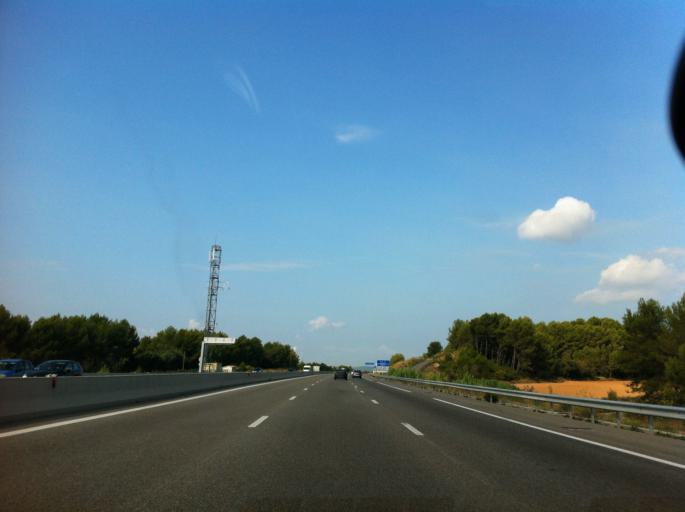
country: FR
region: Provence-Alpes-Cote d'Azur
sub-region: Departement des Bouches-du-Rhone
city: Peynier
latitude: 43.4701
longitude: 5.6526
